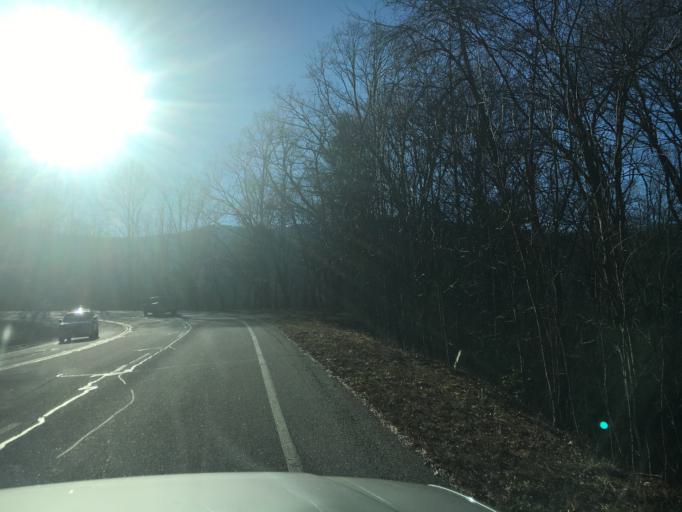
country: US
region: Georgia
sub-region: Union County
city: Blairsville
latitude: 34.7618
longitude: -83.9229
